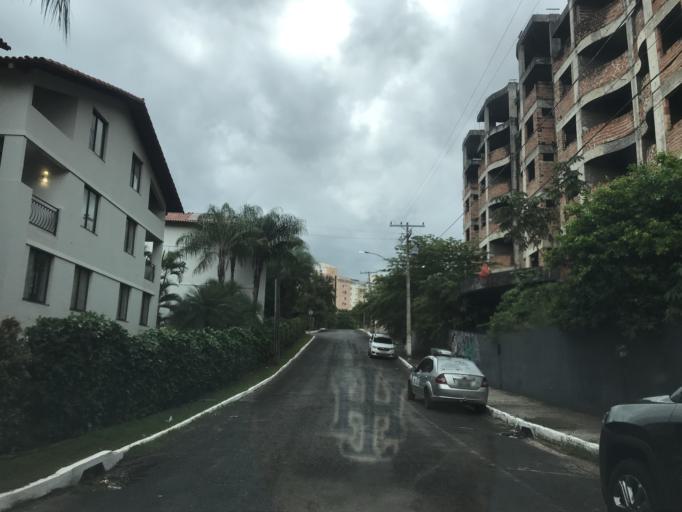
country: BR
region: Goias
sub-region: Caldas Novas
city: Caldas Novas
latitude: -17.7689
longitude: -48.7569
